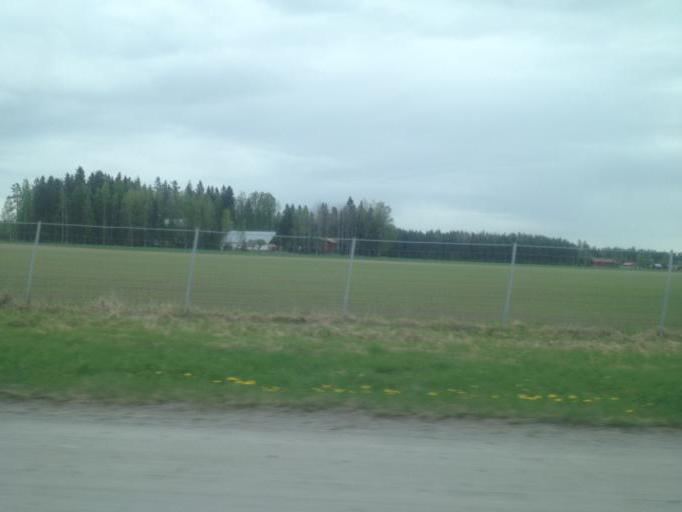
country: FI
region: Uusimaa
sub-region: Helsinki
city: Nurmijaervi
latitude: 60.5152
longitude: 24.8471
